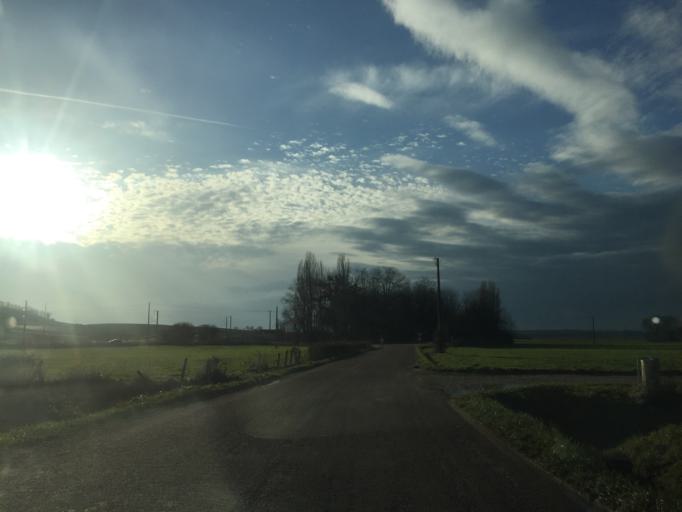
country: FR
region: Franche-Comte
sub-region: Departement du Jura
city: Arbois
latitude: 46.9180
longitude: 5.7452
